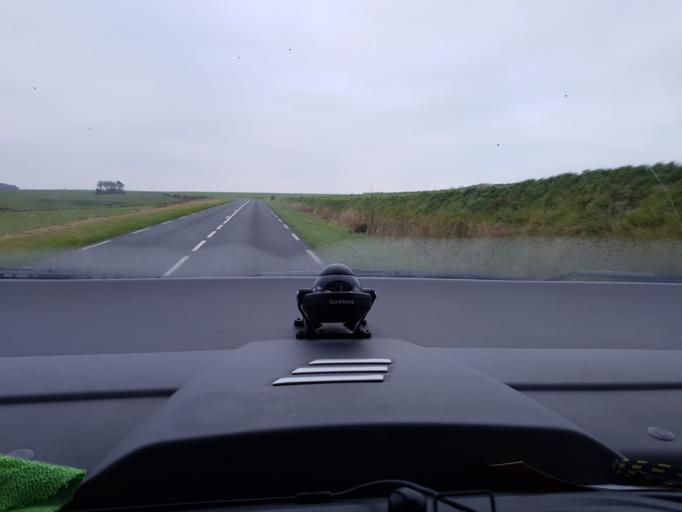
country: FR
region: Picardie
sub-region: Departement de la Somme
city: Ault
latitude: 50.1165
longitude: 1.4809
